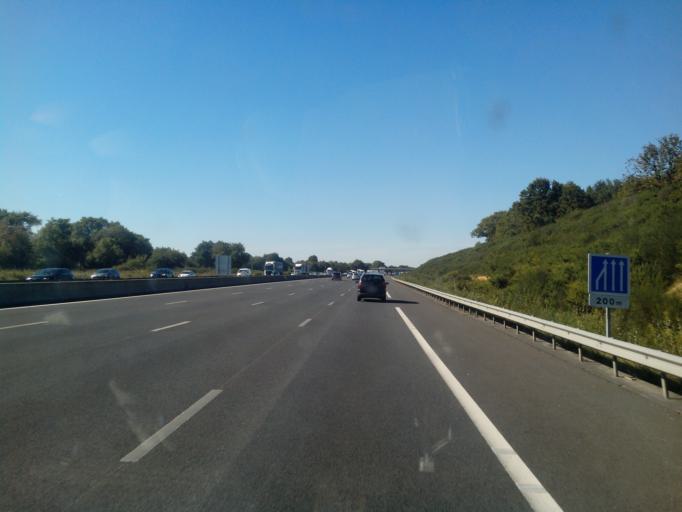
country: FR
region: Pays de la Loire
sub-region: Departement de la Loire-Atlantique
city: Sautron
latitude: 47.2590
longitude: -1.6955
